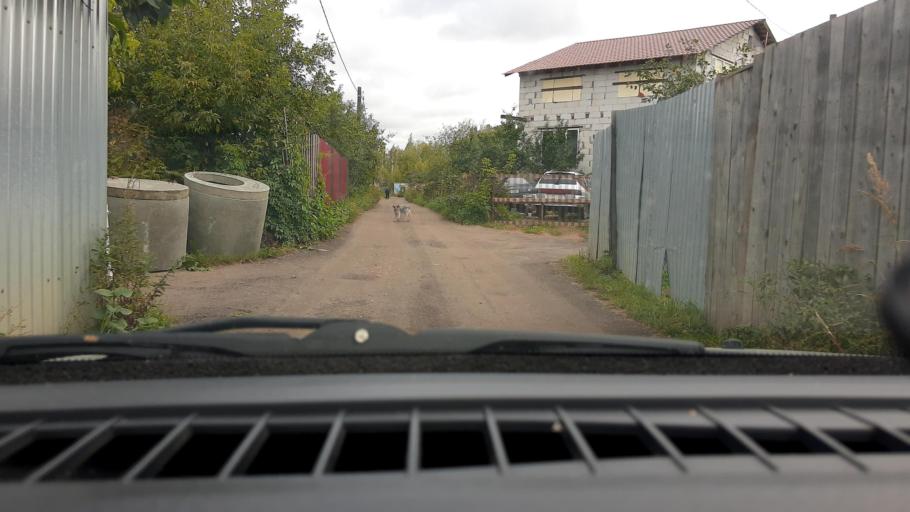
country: RU
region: Nizjnij Novgorod
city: Gorbatovka
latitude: 56.3209
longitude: 43.8382
